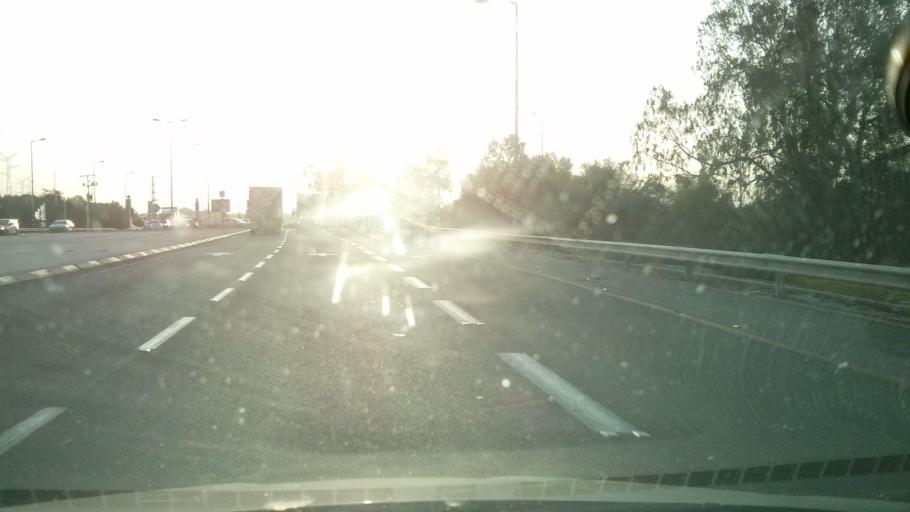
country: IL
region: Haifa
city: Hadera
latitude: 32.4654
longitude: 34.9116
